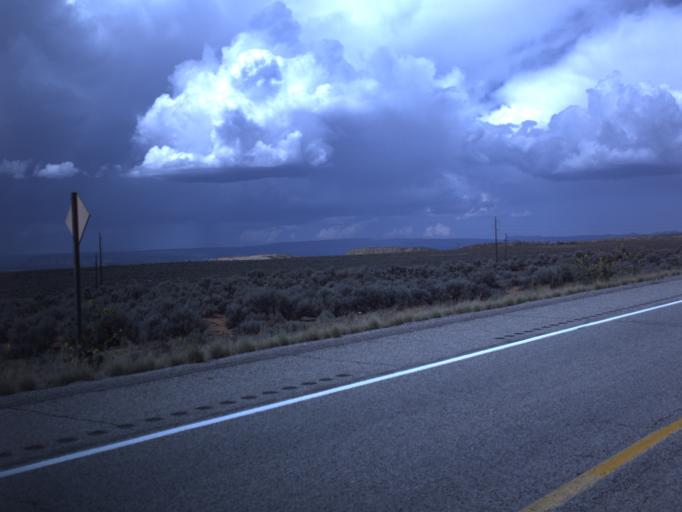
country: US
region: Utah
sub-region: San Juan County
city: Blanding
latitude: 37.5154
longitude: -109.4940
